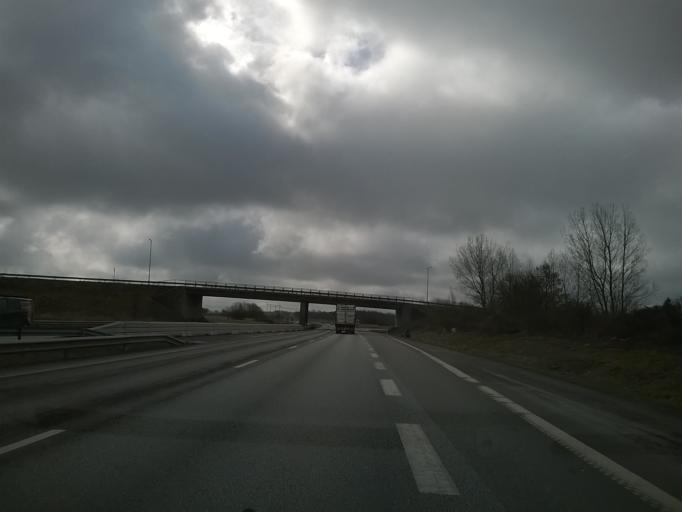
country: SE
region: Halland
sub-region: Varbergs Kommun
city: Varberg
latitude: 57.1296
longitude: 12.3118
